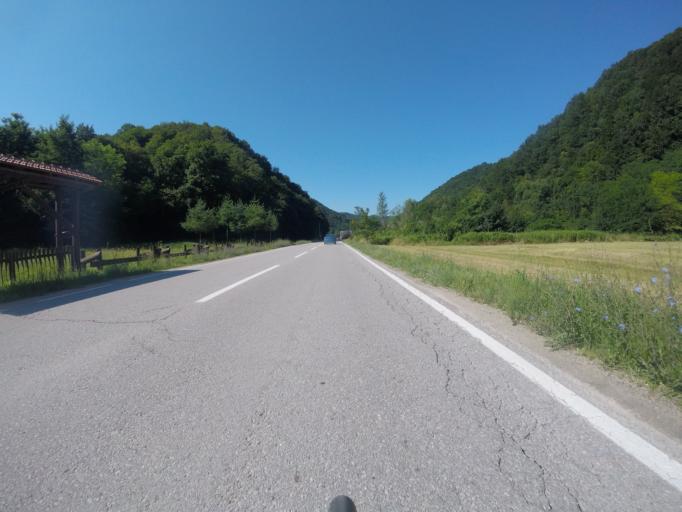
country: HR
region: Zagrebacka
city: Bregana
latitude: 45.8298
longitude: 15.6516
